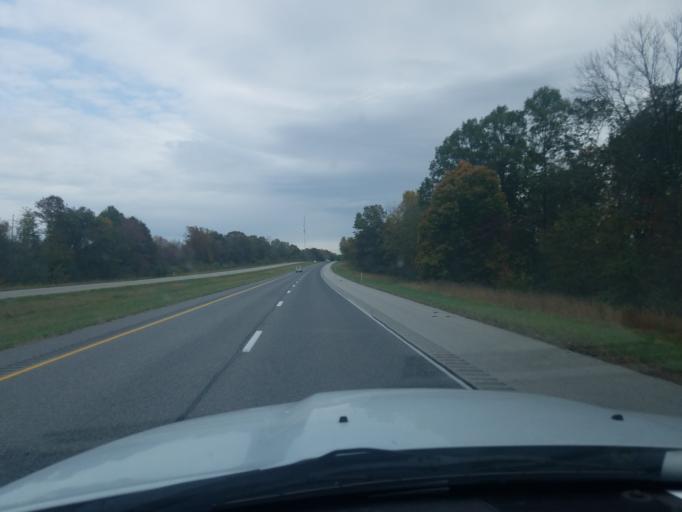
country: US
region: Indiana
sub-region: Warrick County
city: Boonville
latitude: 38.2019
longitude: -87.2127
